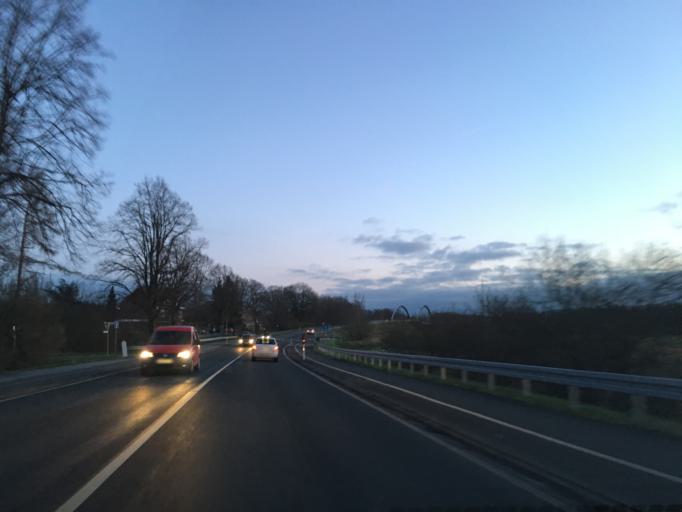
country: DE
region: North Rhine-Westphalia
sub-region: Regierungsbezirk Munster
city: Muenster
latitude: 51.8930
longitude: 7.6457
